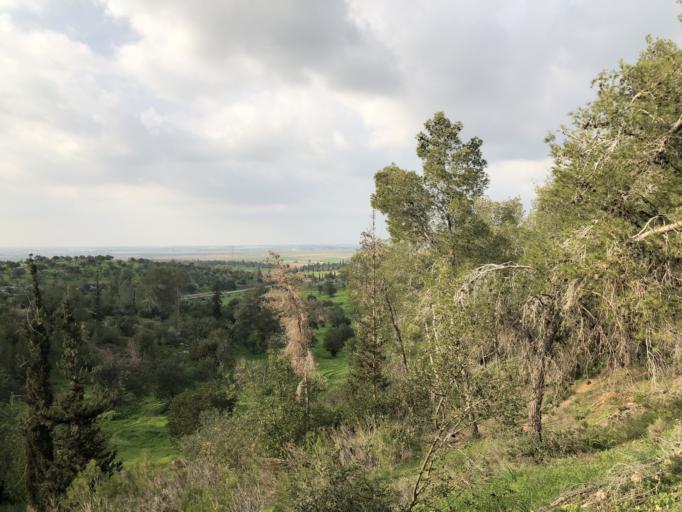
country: IL
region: Central District
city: Gedera
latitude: 31.7321
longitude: 34.8578
